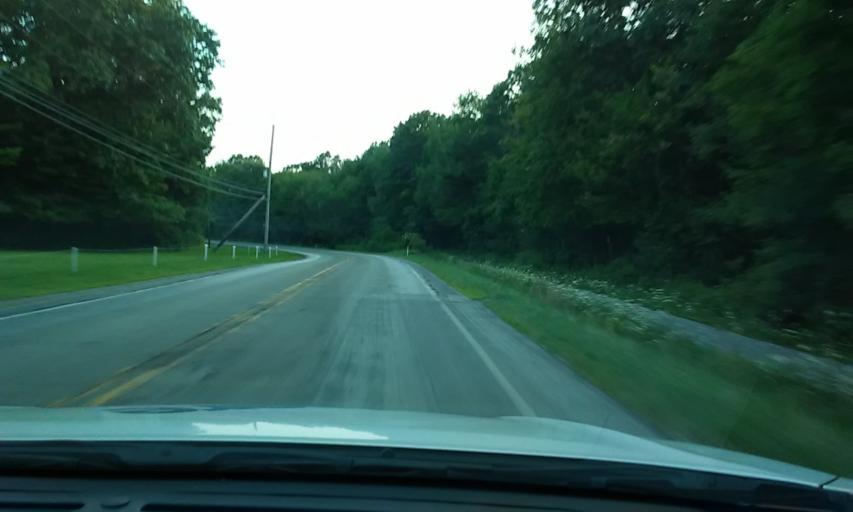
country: US
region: Pennsylvania
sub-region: Clarion County
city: Marianne
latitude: 41.2950
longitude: -79.3823
